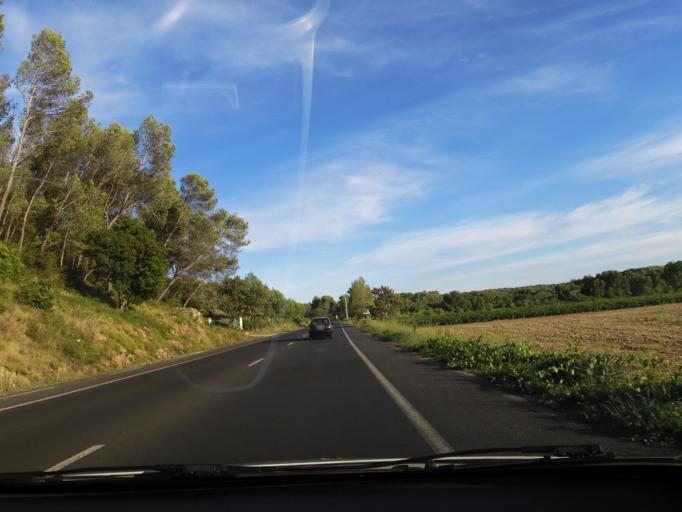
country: FR
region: Languedoc-Roussillon
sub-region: Departement de l'Herault
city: Montferrier-sur-Lez
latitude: 43.6580
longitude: 3.8691
